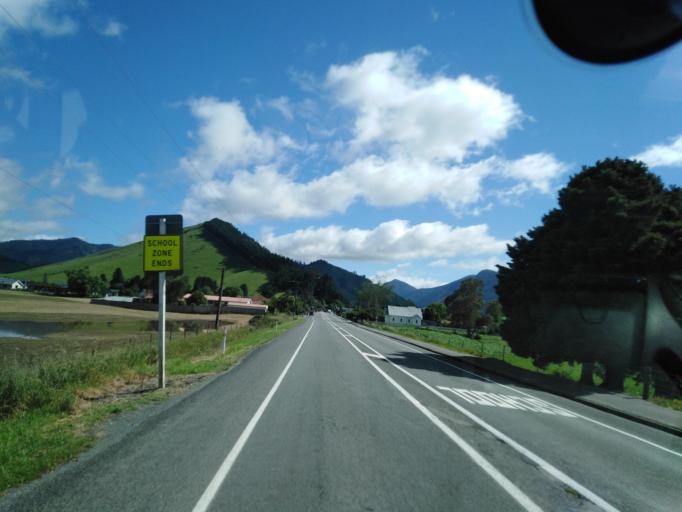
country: NZ
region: Nelson
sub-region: Nelson City
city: Nelson
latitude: -41.2318
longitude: 173.5818
